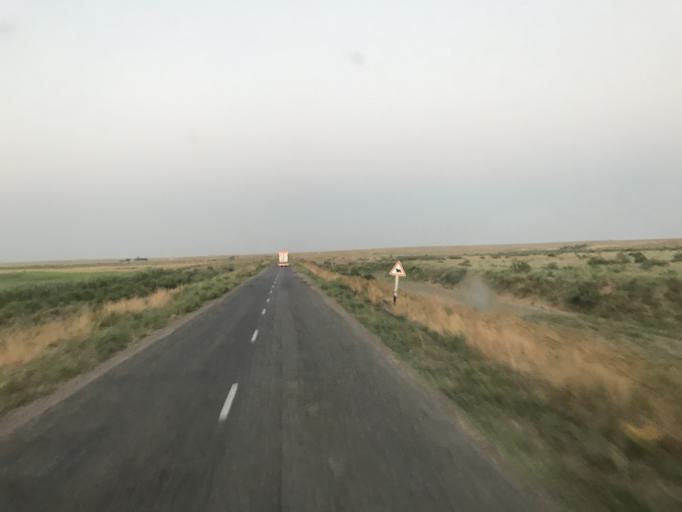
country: UZ
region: Toshkent
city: Chinoz
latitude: 41.2016
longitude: 68.5980
